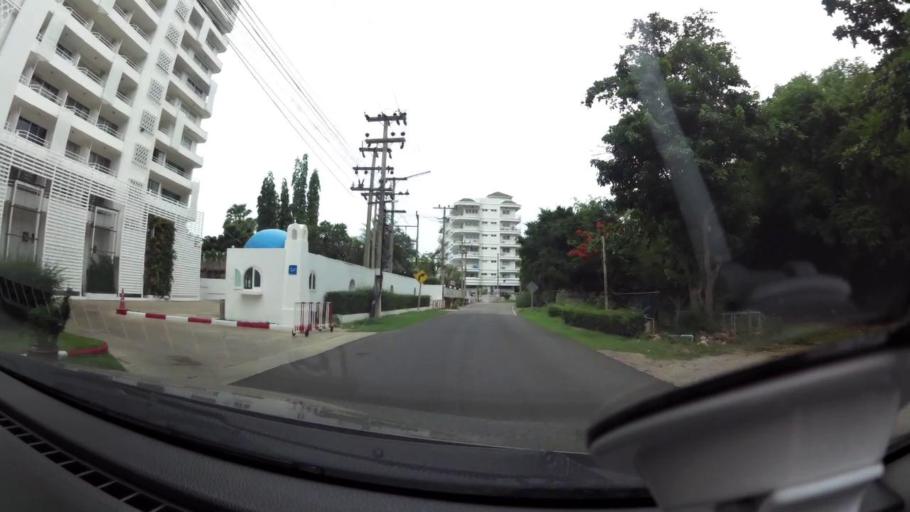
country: TH
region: Prachuap Khiri Khan
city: Pran Buri
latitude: 12.4307
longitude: 99.9790
